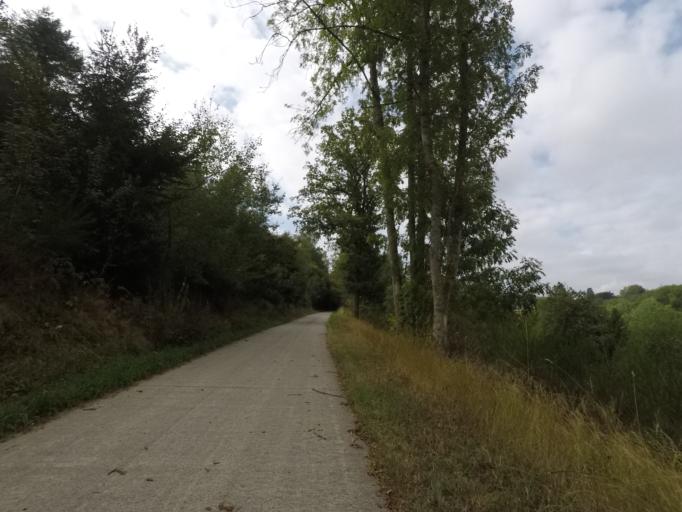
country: BE
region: Wallonia
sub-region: Province du Luxembourg
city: Martelange
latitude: 49.8229
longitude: 5.7503
